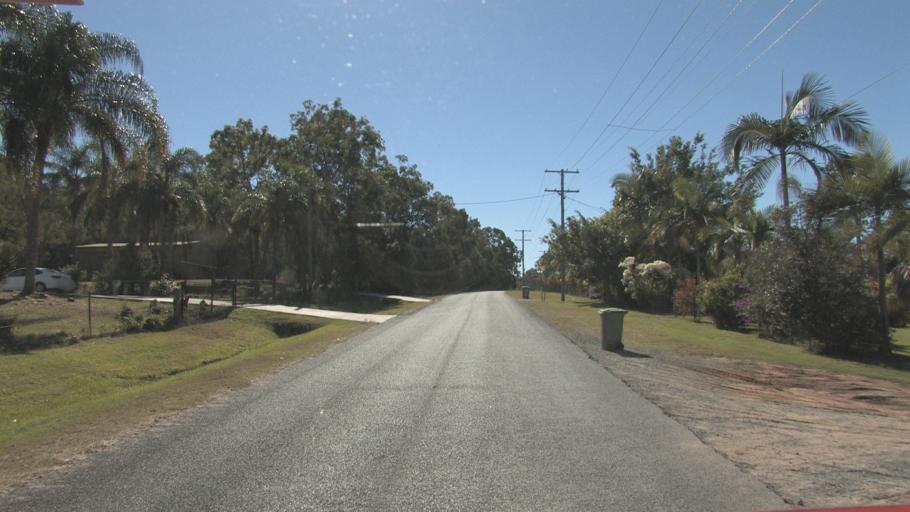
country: AU
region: Queensland
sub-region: Logan
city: Park Ridge South
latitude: -27.7158
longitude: 153.0404
